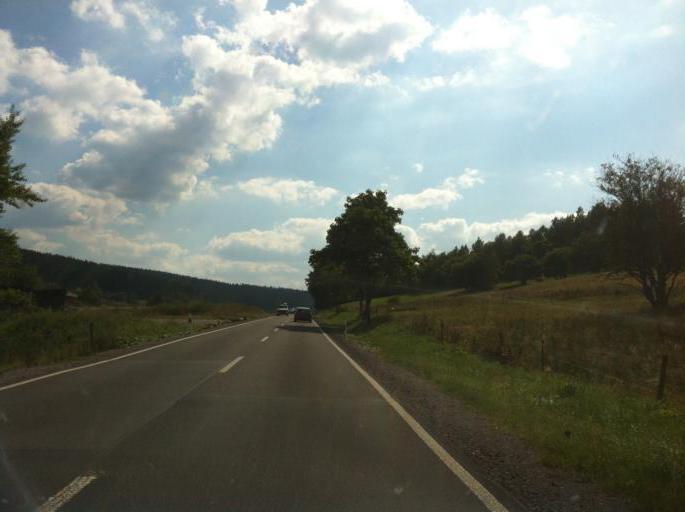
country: DE
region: Thuringia
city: Mohrenbach
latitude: 50.6146
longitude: 10.9934
